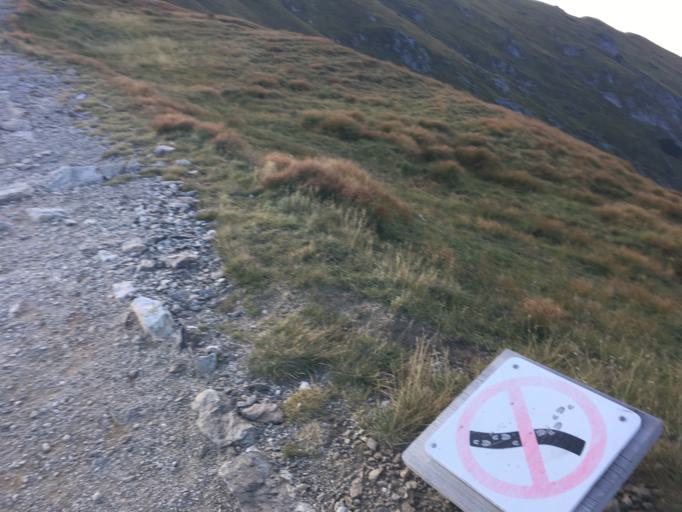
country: PL
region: Lesser Poland Voivodeship
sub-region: Powiat tatrzanski
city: Zakopane
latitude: 49.2346
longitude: 19.9378
